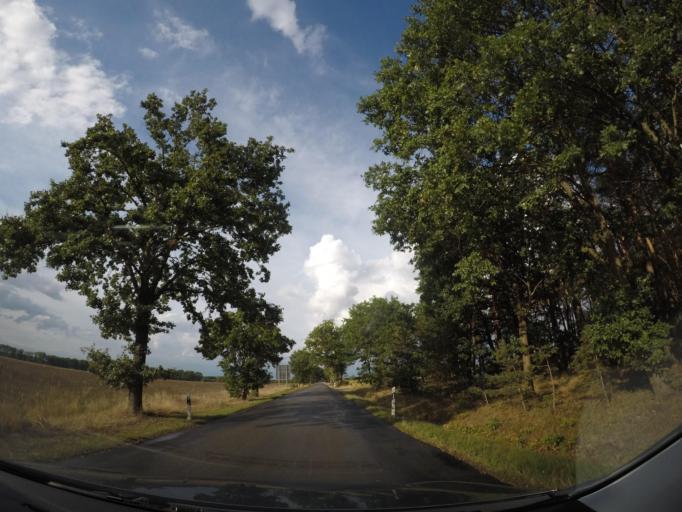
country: DE
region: Saxony-Anhalt
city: Mieste
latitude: 52.5205
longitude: 11.1478
